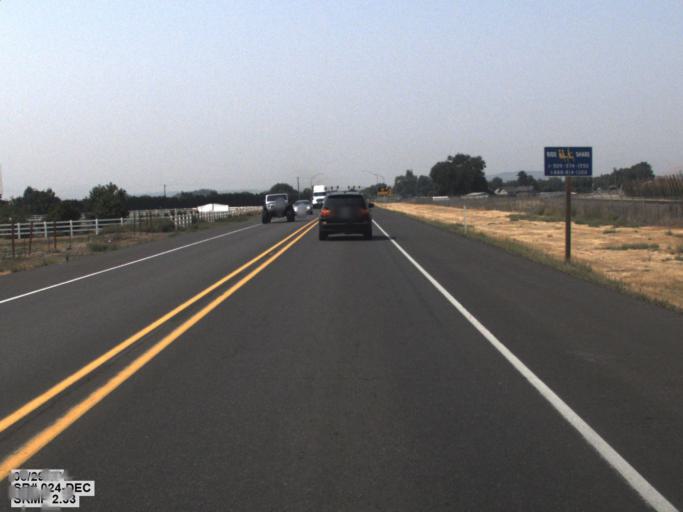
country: US
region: Washington
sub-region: Yakima County
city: Terrace Heights
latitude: 46.5728
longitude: -120.4308
